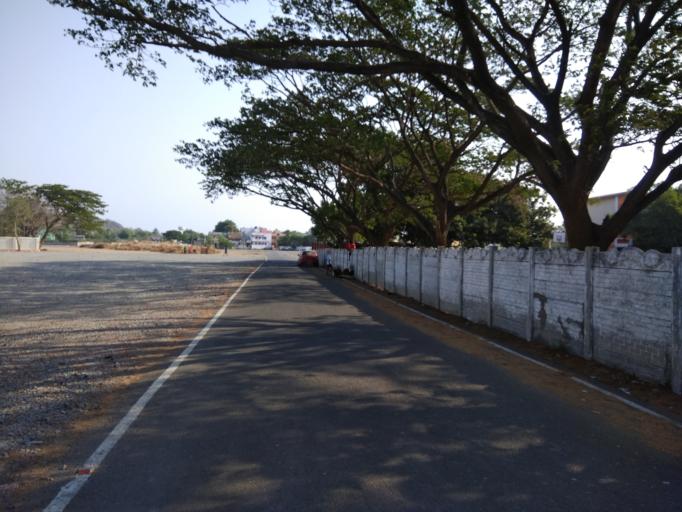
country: IN
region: Tamil Nadu
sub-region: Kancheepuram
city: Saint Thomas Mount
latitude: 13.0144
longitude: 80.1889
